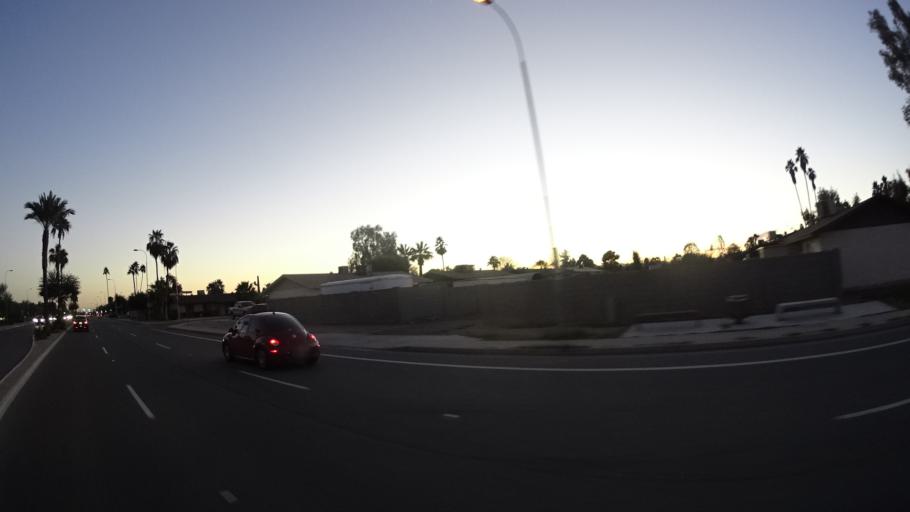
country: US
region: Arizona
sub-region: Maricopa County
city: Chandler
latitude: 33.3018
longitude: -111.8763
